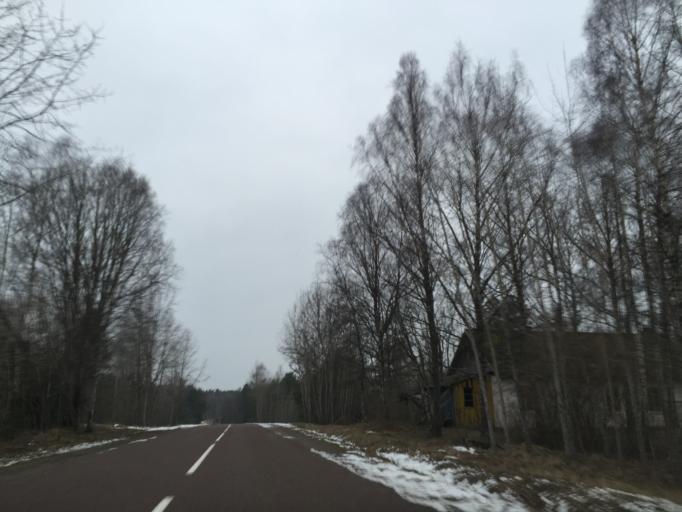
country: EE
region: Saare
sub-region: Kuressaare linn
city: Kuressaare
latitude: 58.3931
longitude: 22.2057
